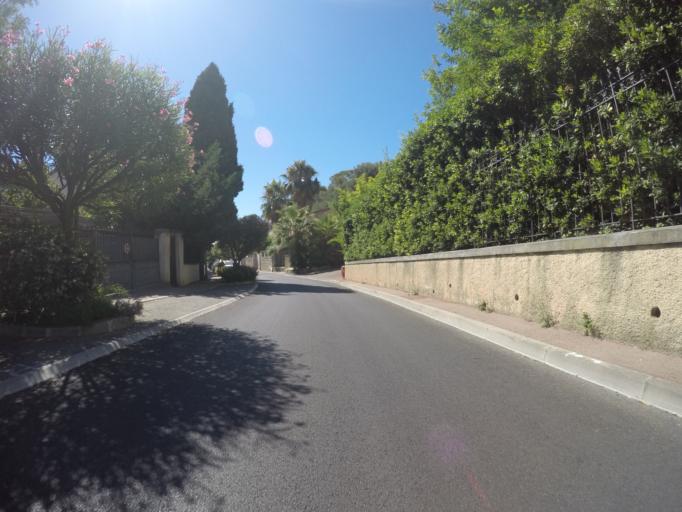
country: FR
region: Provence-Alpes-Cote d'Azur
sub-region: Departement des Alpes-Maritimes
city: Saint-Jean-Cap-Ferrat
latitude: 43.6905
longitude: 7.3301
